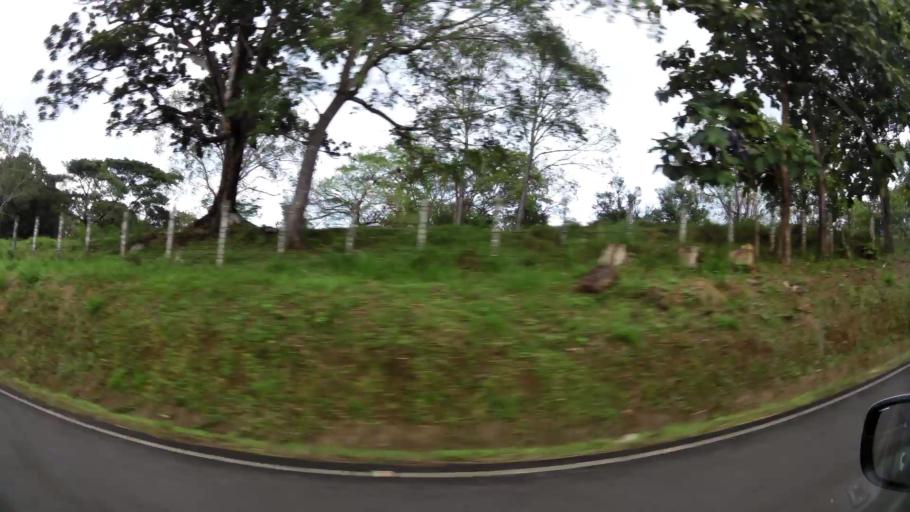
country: CR
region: Puntarenas
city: Esparza
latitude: 9.9945
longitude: -84.6513
